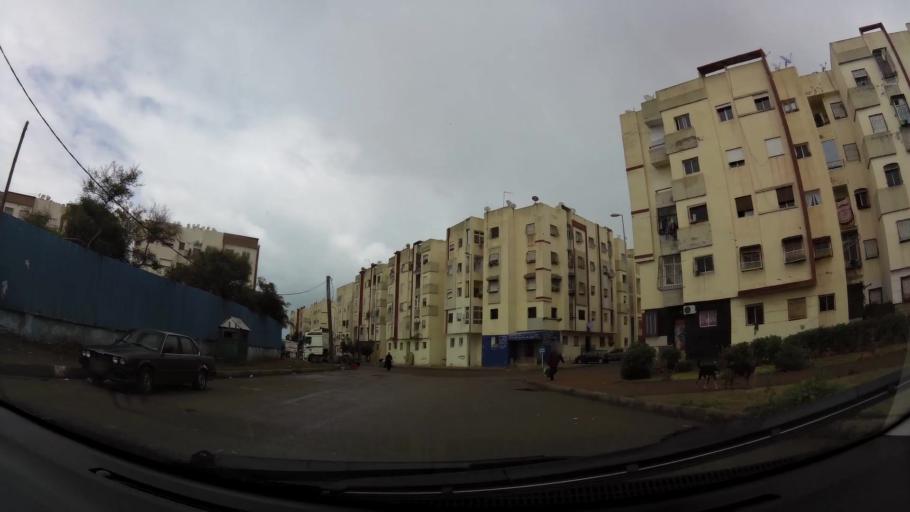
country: MA
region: Grand Casablanca
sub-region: Casablanca
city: Casablanca
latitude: 33.5499
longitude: -7.6931
